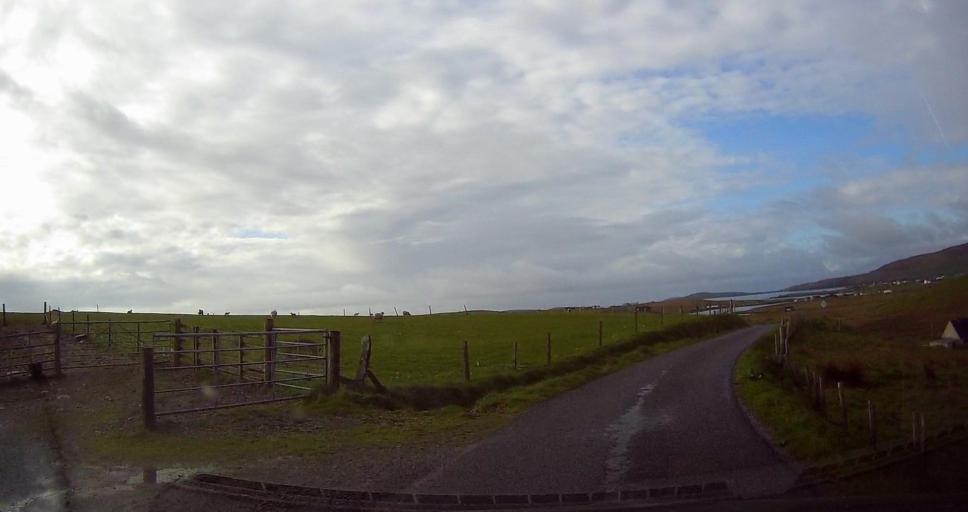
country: GB
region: Scotland
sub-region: Shetland Islands
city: Sandwick
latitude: 60.0534
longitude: -1.2076
